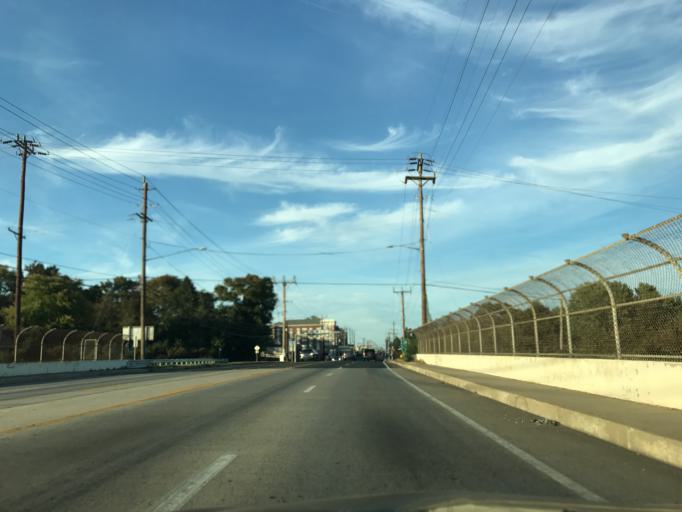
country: US
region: Maryland
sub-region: Prince George's County
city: College Park
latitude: 39.0012
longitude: -76.9311
